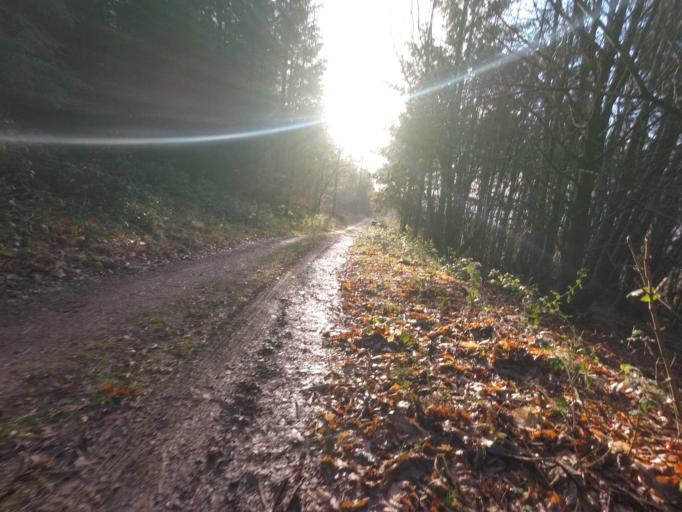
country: IE
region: Munster
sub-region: Waterford
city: Portlaw
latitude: 52.3139
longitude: -7.3482
